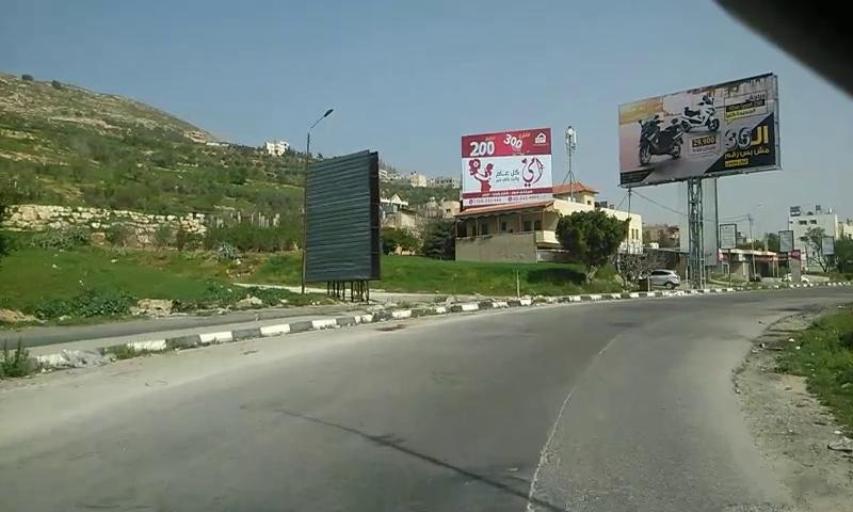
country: PS
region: West Bank
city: Kafr Qallil
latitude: 32.1831
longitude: 35.2772
